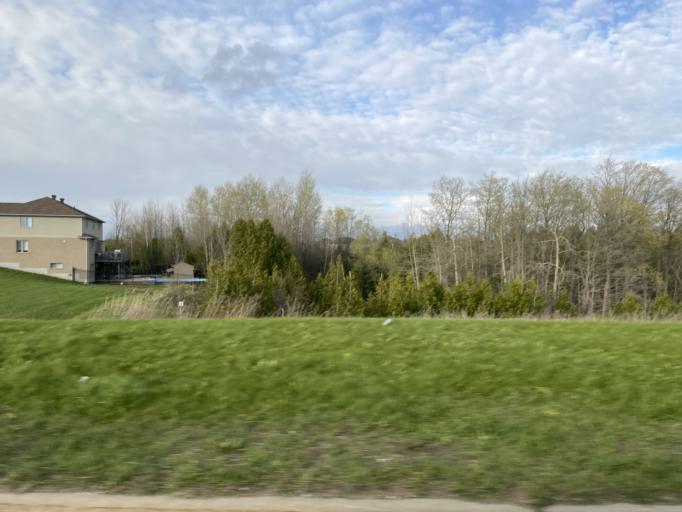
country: CA
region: Ontario
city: Waterloo
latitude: 43.4838
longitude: -80.4120
